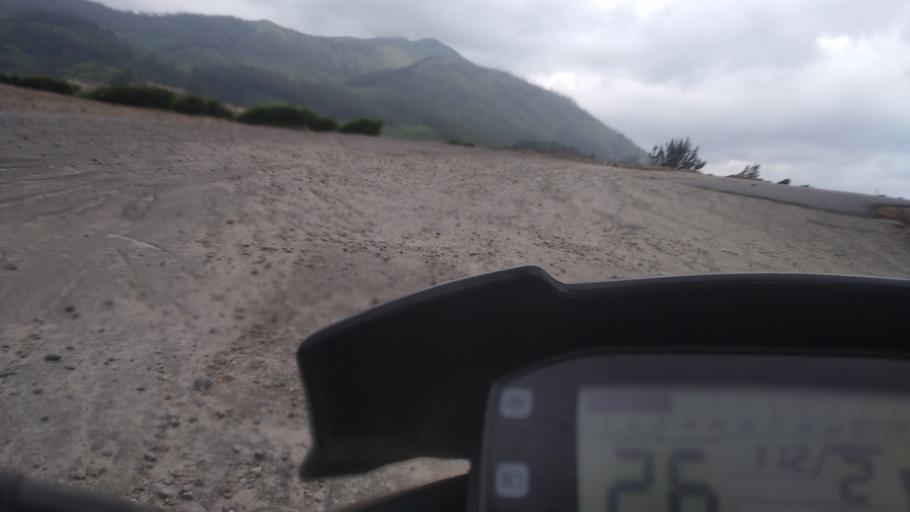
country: IN
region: Kerala
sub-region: Idukki
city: Munnar
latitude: 10.0813
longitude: 77.0766
